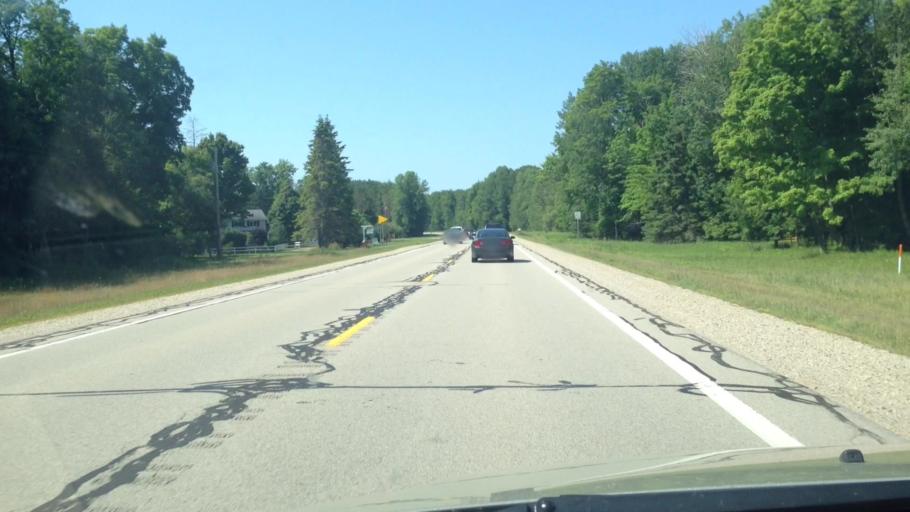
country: US
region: Michigan
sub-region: Menominee County
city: Menominee
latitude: 45.3712
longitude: -87.3914
